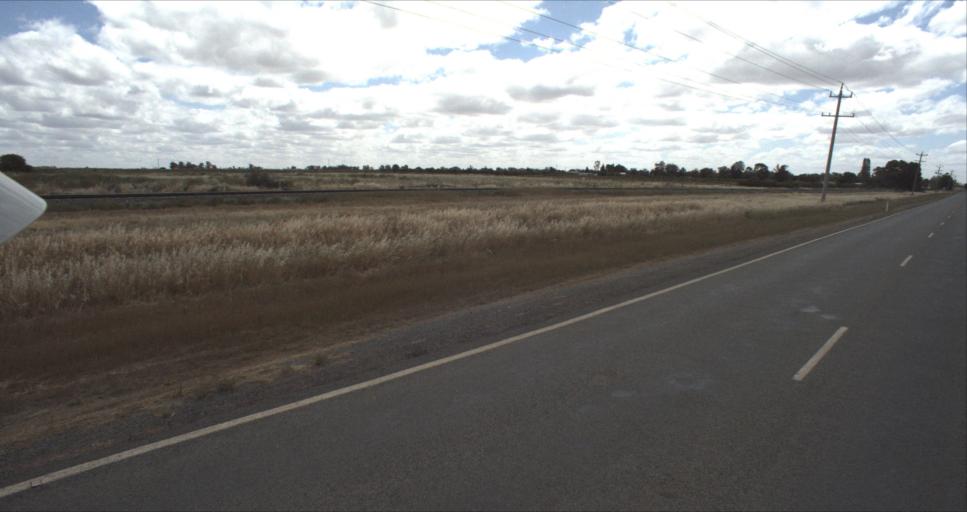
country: AU
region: New South Wales
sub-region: Leeton
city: Leeton
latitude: -34.5753
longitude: 146.3952
